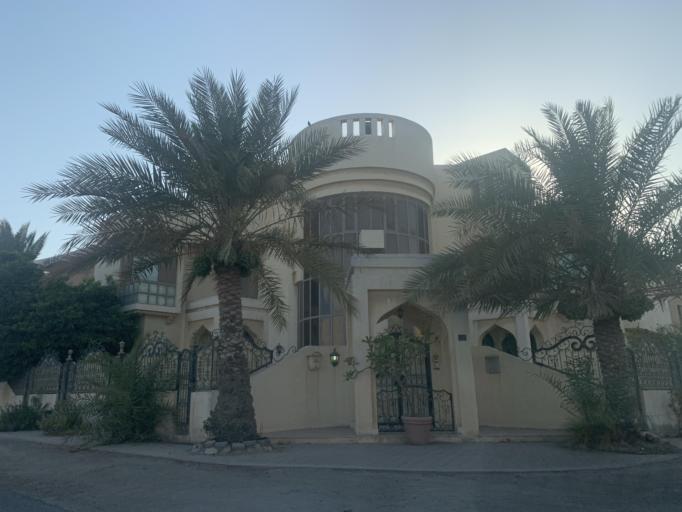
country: BH
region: Manama
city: Jidd Hafs
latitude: 26.2098
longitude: 50.5306
